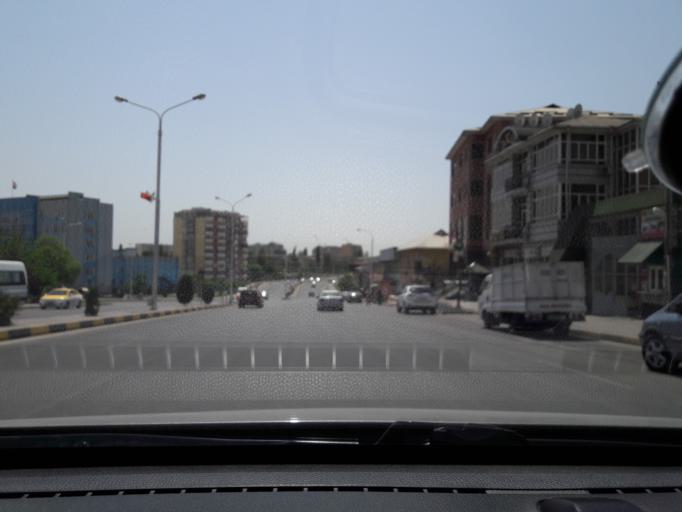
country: TJ
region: Dushanbe
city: Dushanbe
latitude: 38.5870
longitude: 68.7151
